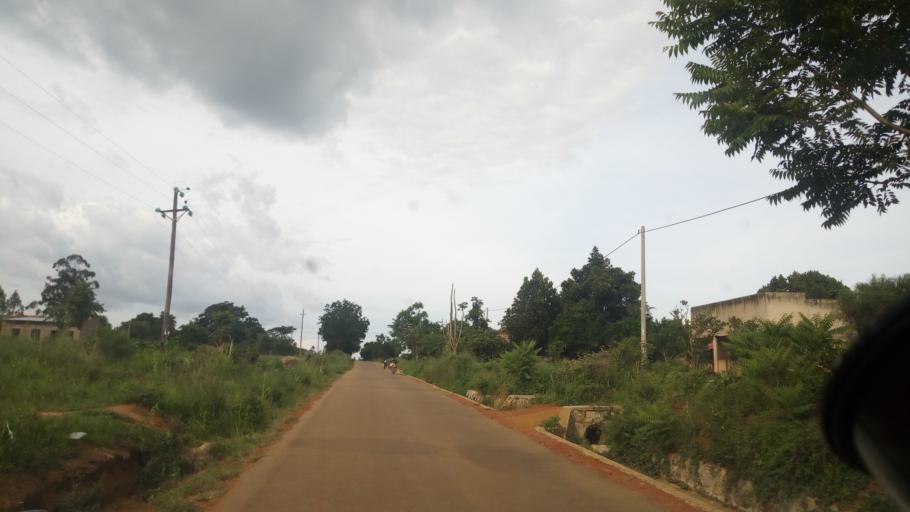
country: UG
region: Northern Region
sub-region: Lira District
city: Lira
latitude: 2.2536
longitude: 32.8433
